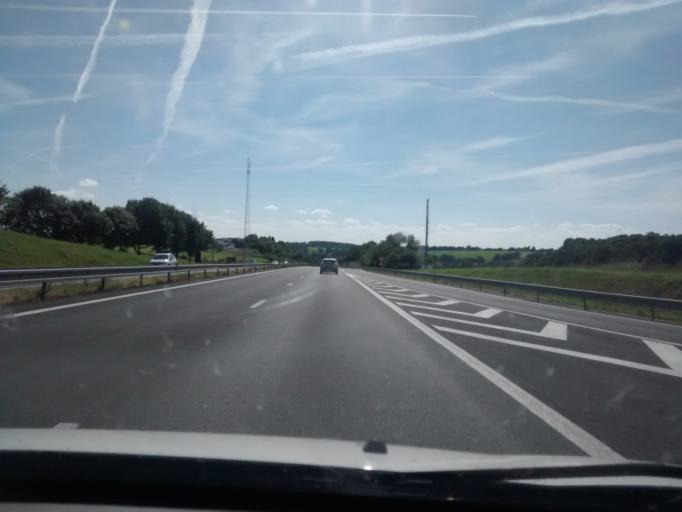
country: FR
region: Pays de la Loire
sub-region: Departement de la Sarthe
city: Loue
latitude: 48.0073
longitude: -0.1620
